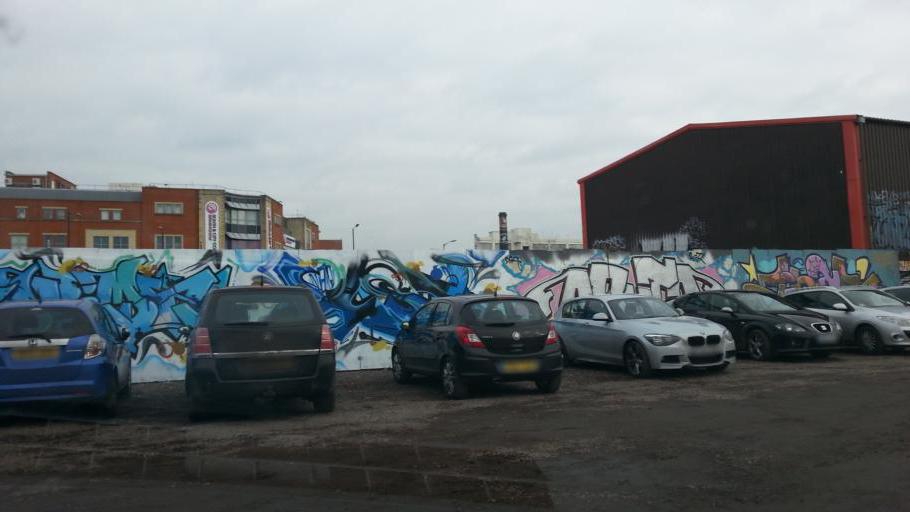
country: GB
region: England
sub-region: City and Borough of Birmingham
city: Birmingham
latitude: 52.4743
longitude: -1.8873
